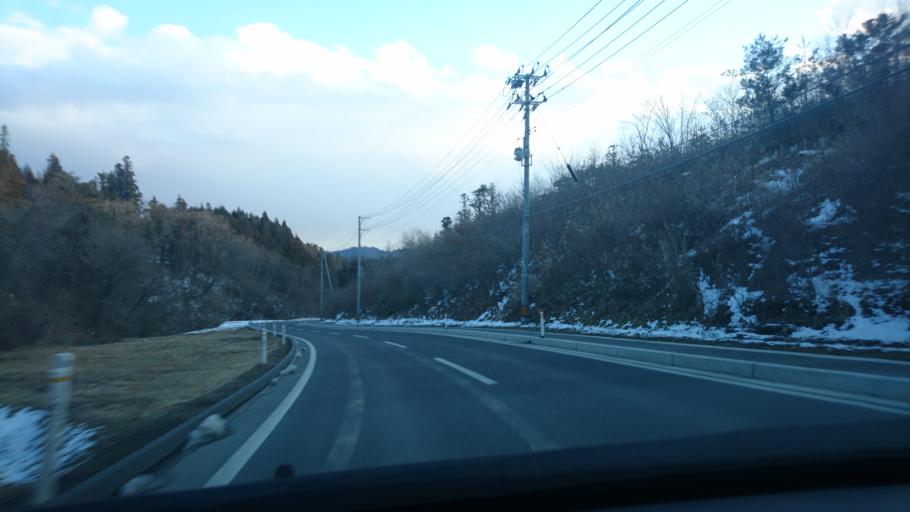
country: JP
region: Iwate
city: Ichinoseki
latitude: 39.0032
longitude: 141.3329
